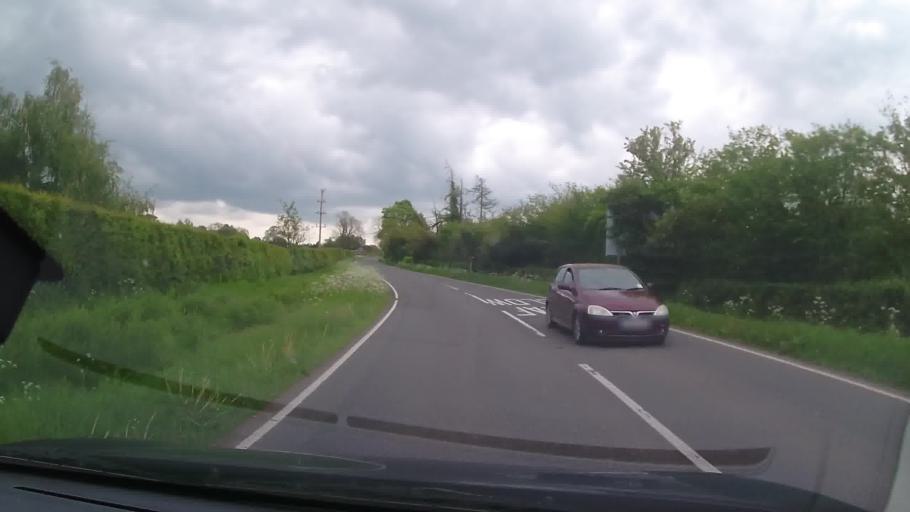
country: GB
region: Wales
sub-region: Wrexham
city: Overton
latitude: 52.9594
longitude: -2.9399
